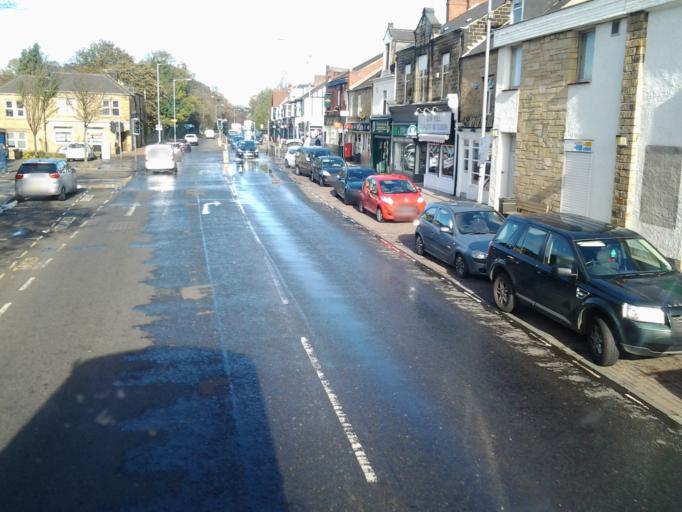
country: GB
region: England
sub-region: Gateshead
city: Lamesley
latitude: 54.9364
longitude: -1.5996
